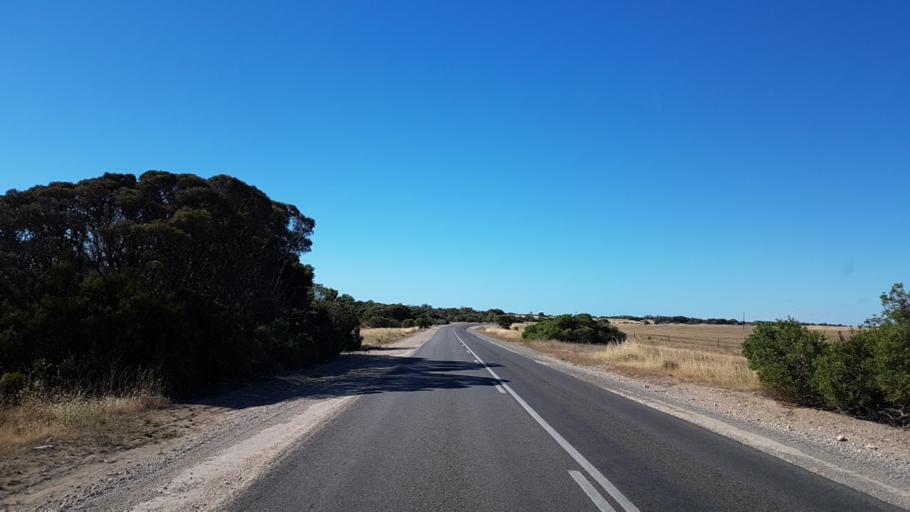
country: AU
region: South Australia
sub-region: Yorke Peninsula
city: Honiton
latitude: -34.9157
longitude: 137.4529
